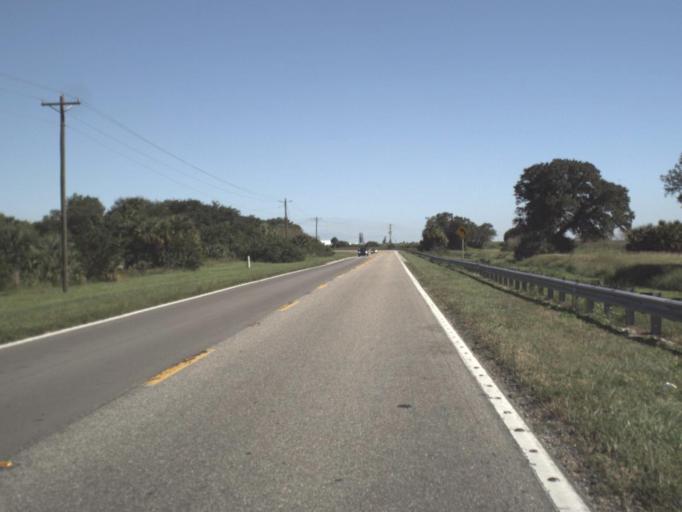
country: US
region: Florida
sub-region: Glades County
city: Moore Haven
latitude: 26.7543
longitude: -81.1489
